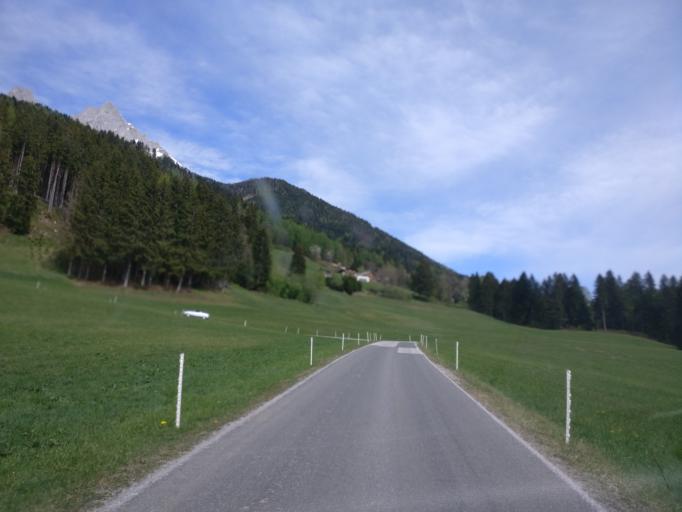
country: AT
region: Salzburg
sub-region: Politischer Bezirk Sankt Johann im Pongau
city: Pfarrwerfen
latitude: 47.4714
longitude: 13.2079
